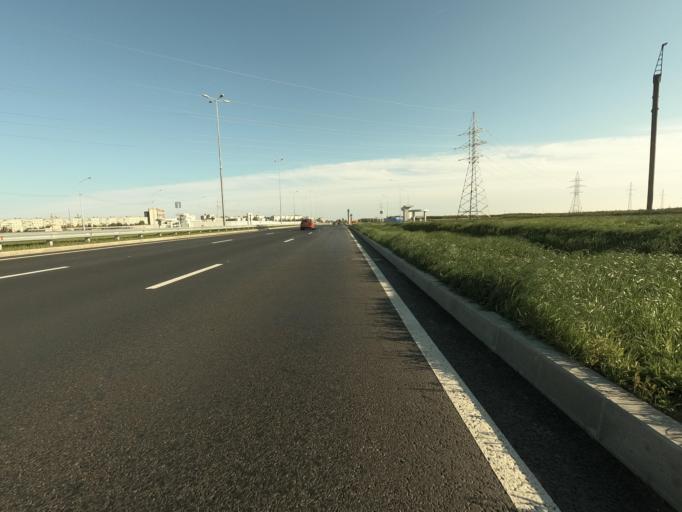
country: RU
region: St.-Petersburg
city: Kolpino
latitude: 59.7406
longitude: 30.5472
